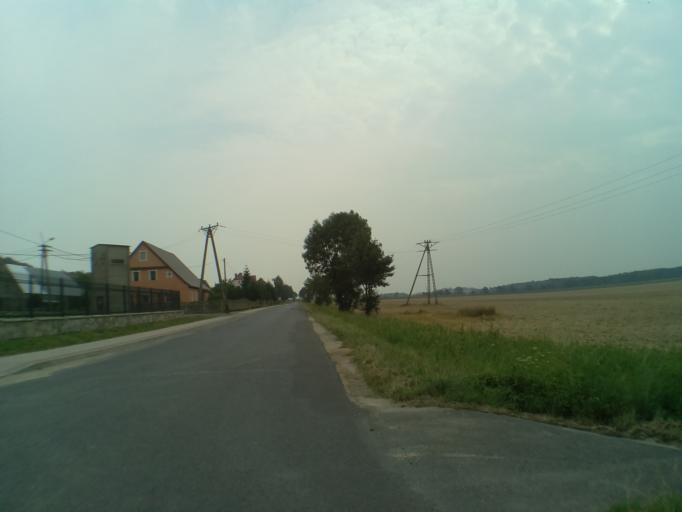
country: PL
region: Lower Silesian Voivodeship
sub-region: Powiat swidnicki
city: Strzegom
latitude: 50.9759
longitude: 16.2876
